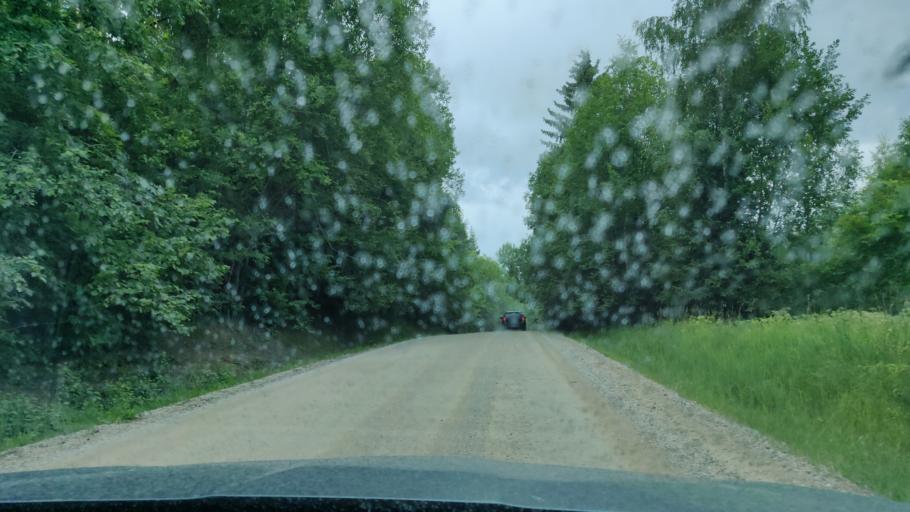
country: EE
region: Vorumaa
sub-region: Antsla vald
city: Vana-Antsla
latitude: 58.0194
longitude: 26.5780
